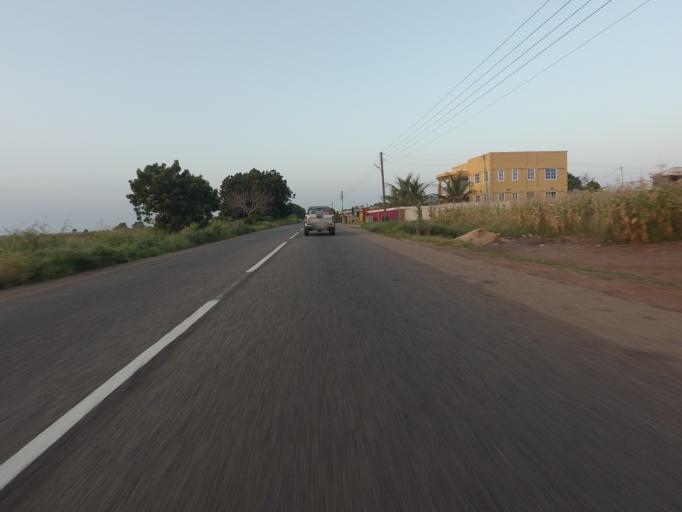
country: GH
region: Volta
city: Anloga
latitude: 5.8180
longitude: 0.9418
